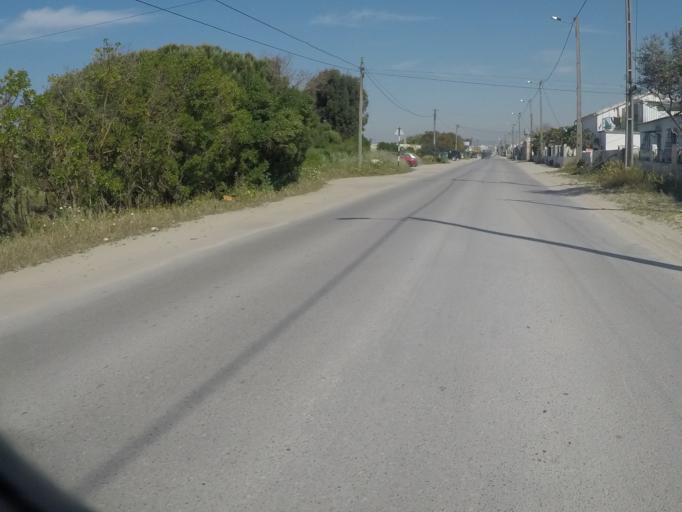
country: PT
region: Setubal
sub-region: Almada
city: Costa de Caparica
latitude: 38.6304
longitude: -9.2224
